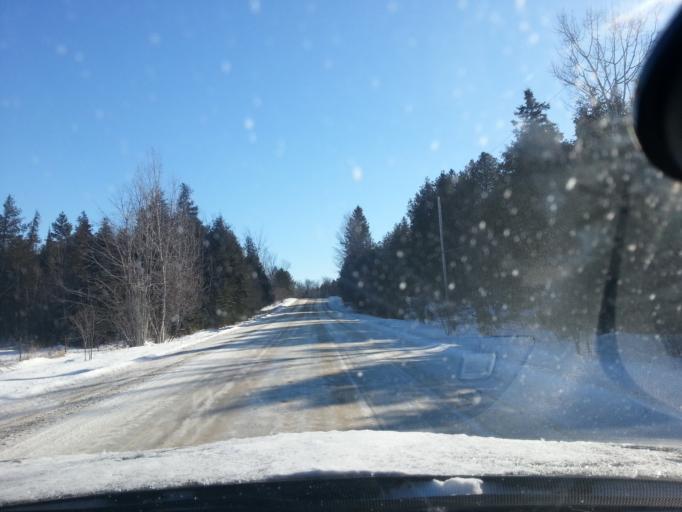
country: CA
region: Ontario
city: Arnprior
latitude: 45.2498
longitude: -76.3106
